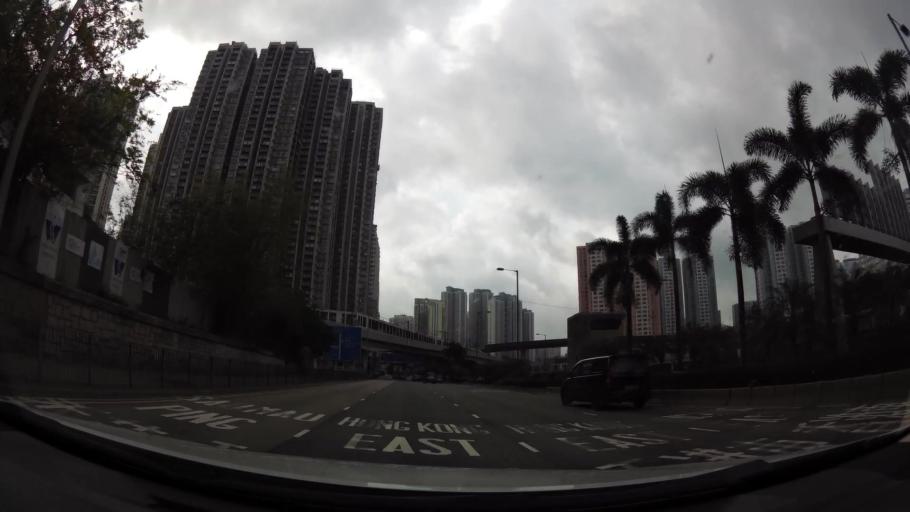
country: HK
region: Kowloon City
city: Kowloon
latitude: 22.3281
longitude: 114.2130
